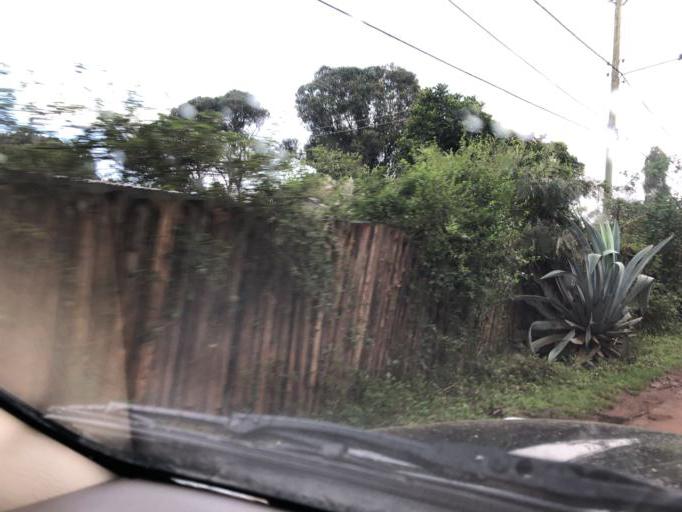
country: KE
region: Kajiado
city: Ngong
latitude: -1.3729
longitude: 36.7443
